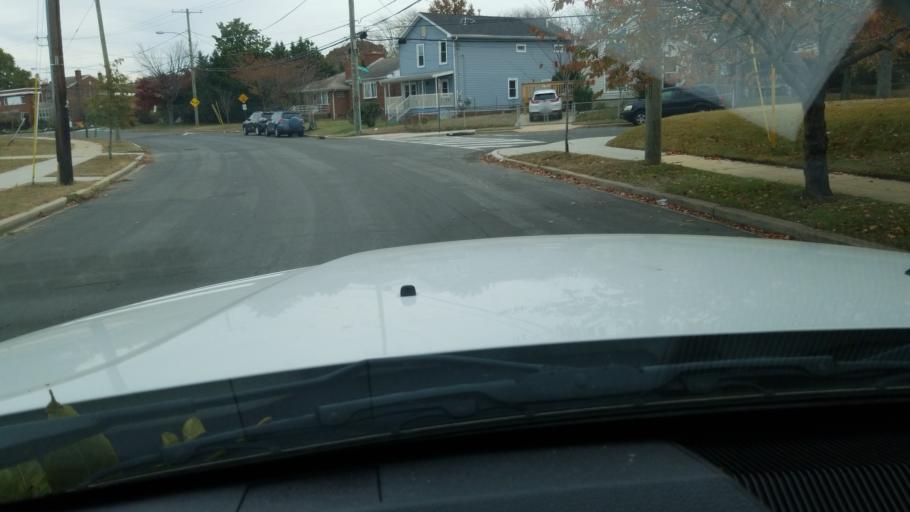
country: US
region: Maryland
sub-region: Prince George's County
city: Colmar Manor
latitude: 38.9067
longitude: -76.9438
